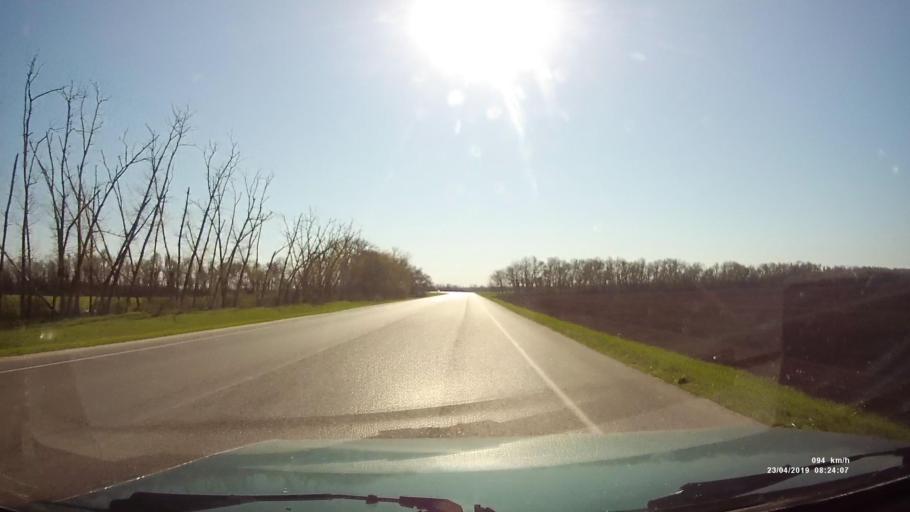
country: RU
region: Rostov
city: Tselina
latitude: 46.5309
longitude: 40.9419
